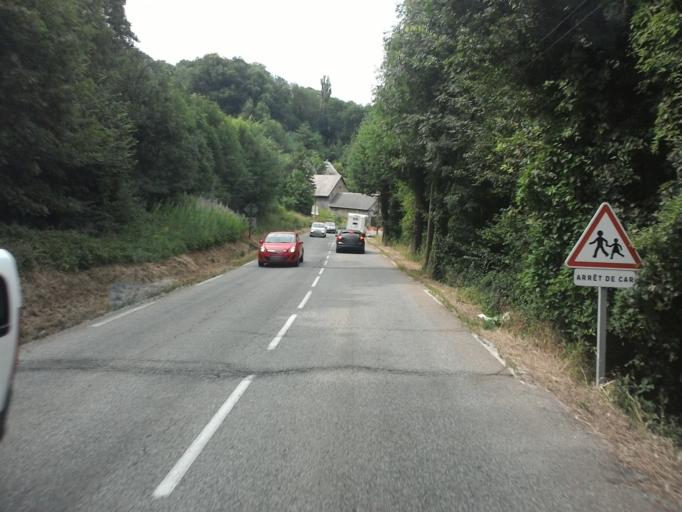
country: FR
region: Rhone-Alpes
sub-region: Departement de l'Isere
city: La Mure
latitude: 44.8984
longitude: 5.8079
